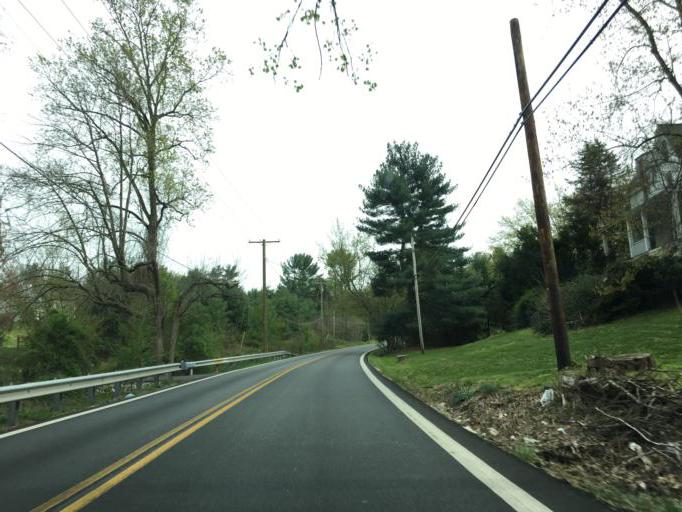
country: US
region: Maryland
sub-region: Baltimore County
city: Hunt Valley
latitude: 39.4946
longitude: -76.5678
